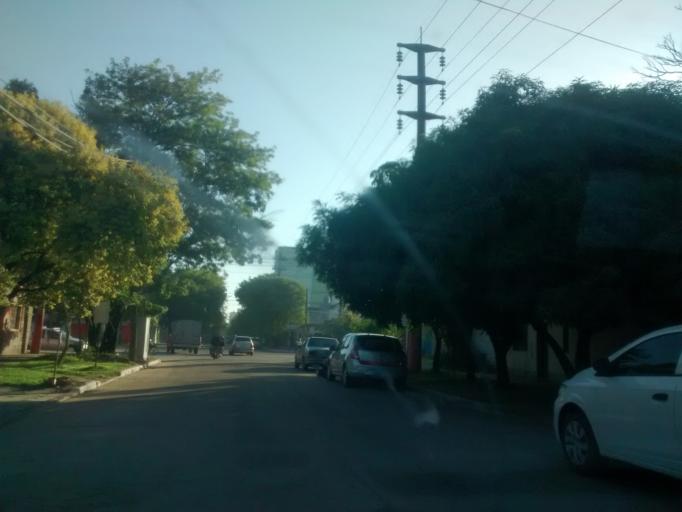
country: AR
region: Chaco
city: Resistencia
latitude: -27.4602
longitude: -58.9914
